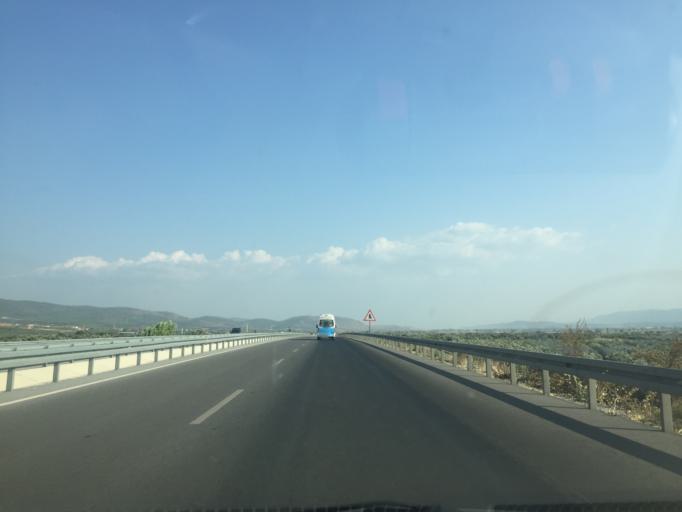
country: TR
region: Manisa
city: Akhisar
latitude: 38.8349
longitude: 27.8656
